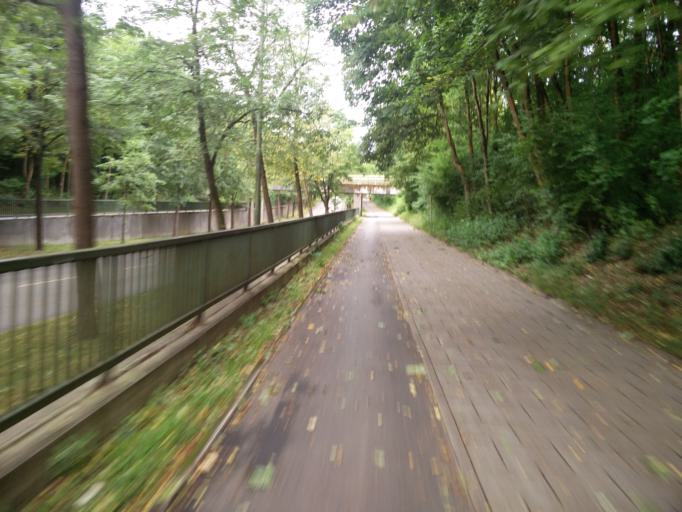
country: DE
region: Bavaria
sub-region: Upper Bavaria
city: Neubiberg
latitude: 48.0923
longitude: 11.6416
